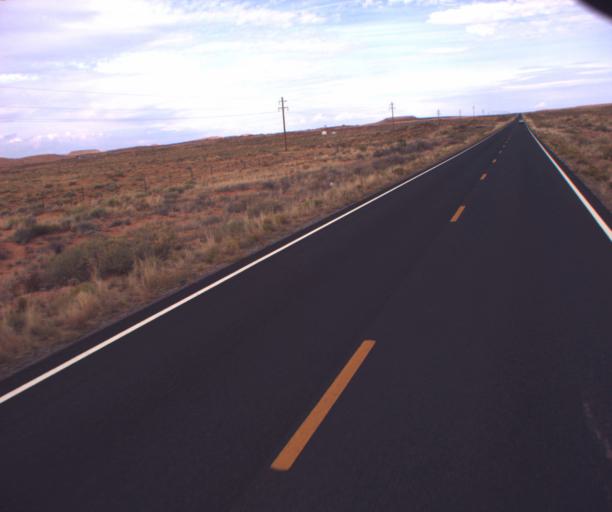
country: US
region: Arizona
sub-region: Apache County
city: Many Farms
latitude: 36.7991
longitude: -109.6490
